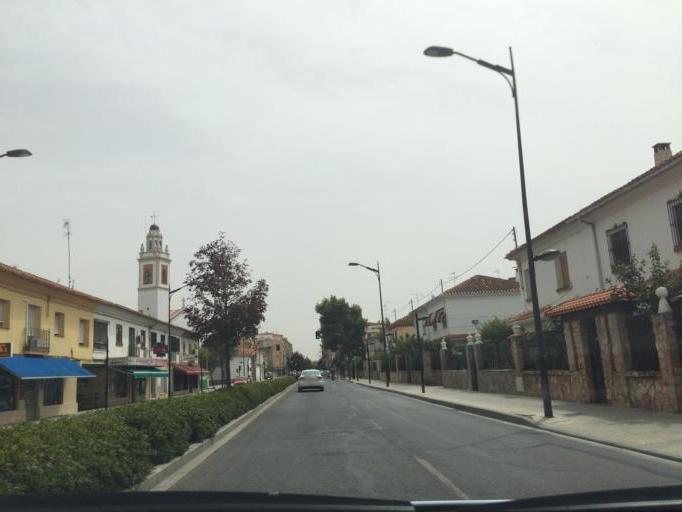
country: ES
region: Castille-La Mancha
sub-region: Provincia de Albacete
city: Albacete
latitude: 38.9931
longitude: -1.8704
